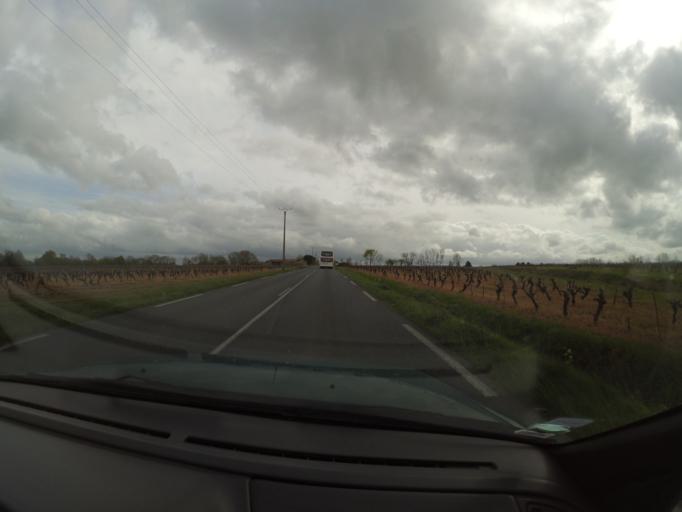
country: FR
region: Pays de la Loire
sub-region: Departement de Maine-et-Loire
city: Lire
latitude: 47.3173
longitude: -1.1636
